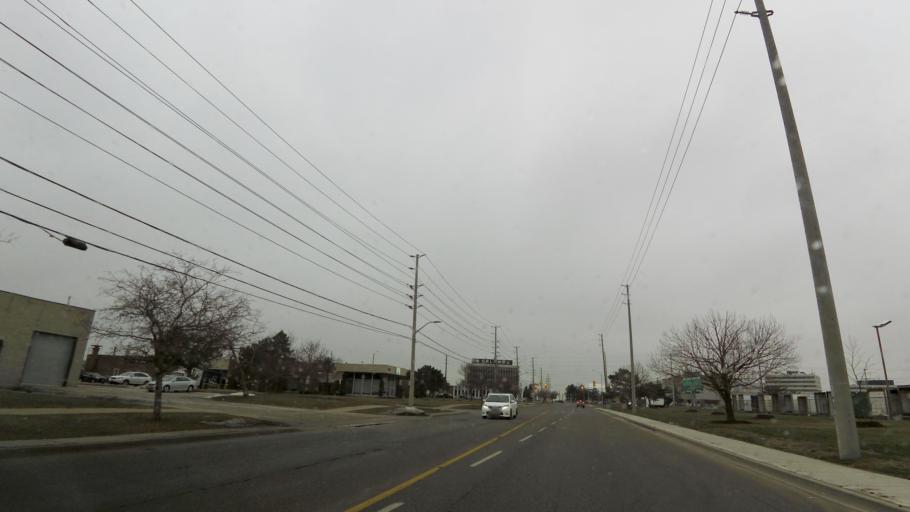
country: CA
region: Ontario
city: Etobicoke
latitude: 43.6927
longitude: -79.6179
